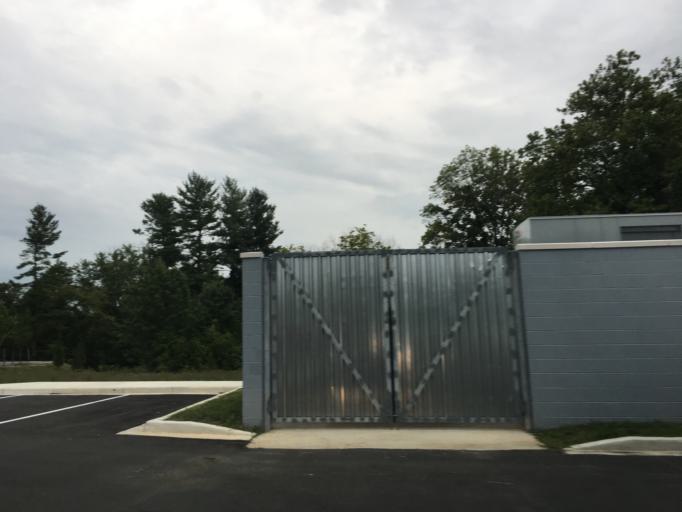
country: US
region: Maryland
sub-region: Baltimore County
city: Cockeysville
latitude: 39.4903
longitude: -76.6513
